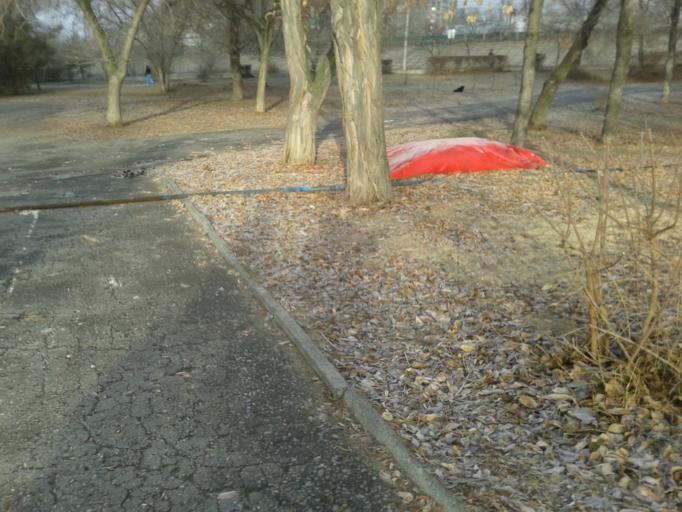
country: RU
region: Volgograd
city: Volgograd
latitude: 48.7094
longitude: 44.5056
